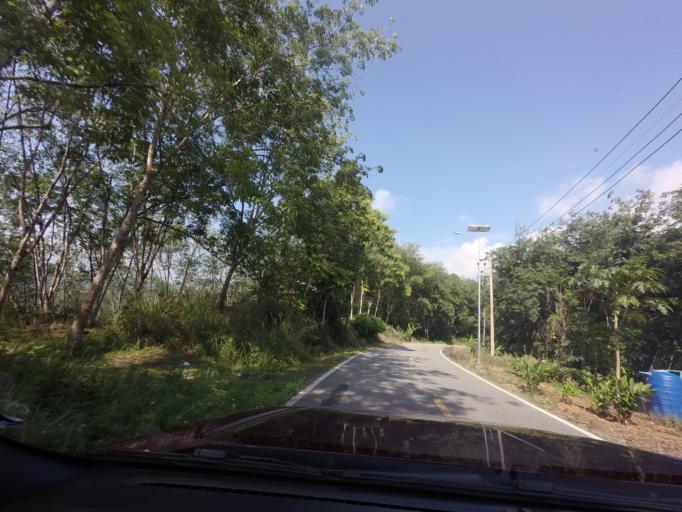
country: TH
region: Yala
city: Than To
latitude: 5.9962
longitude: 101.2153
